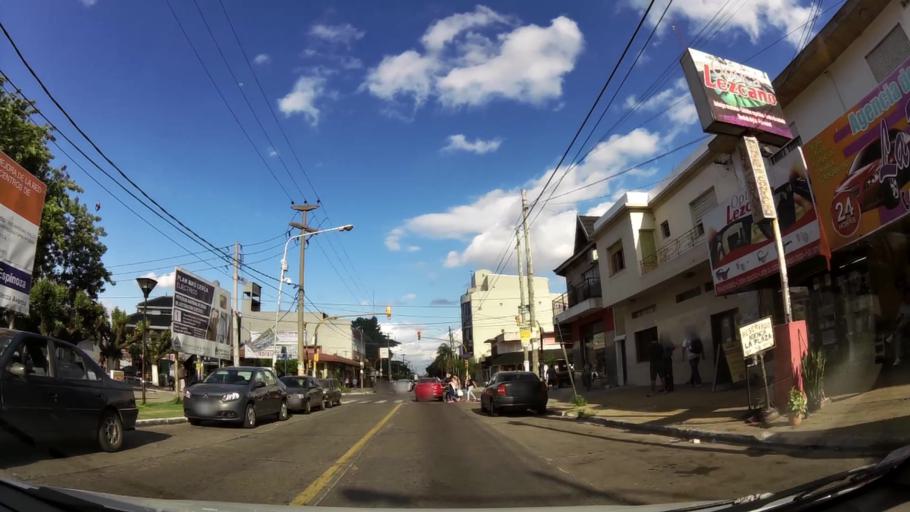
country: AR
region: Buenos Aires
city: San Justo
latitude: -34.7005
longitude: -58.5872
